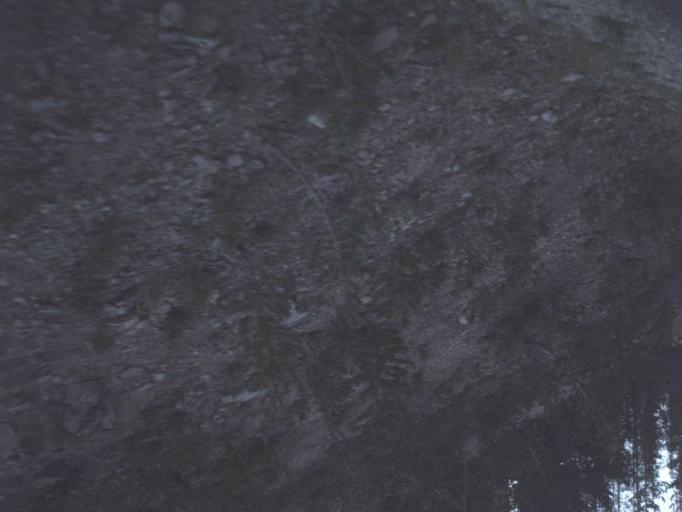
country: US
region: Utah
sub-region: Summit County
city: Kamas
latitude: 40.7608
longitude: -110.8819
